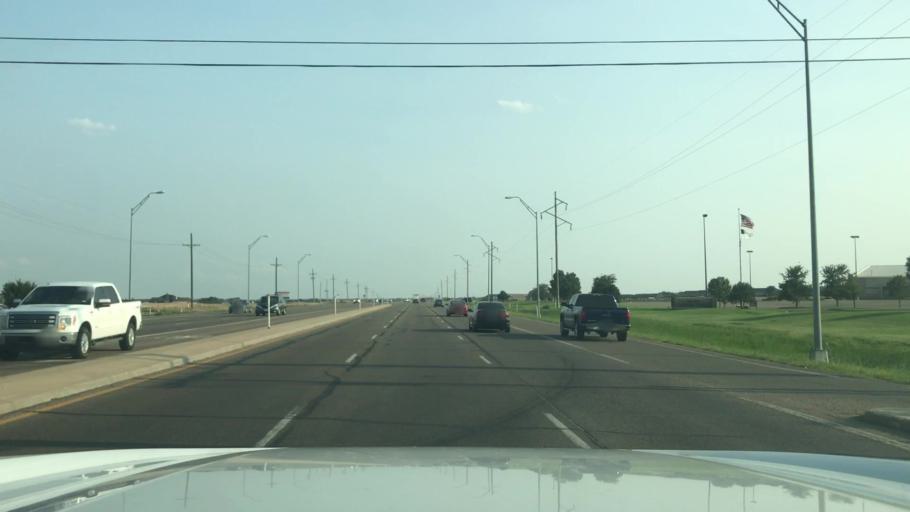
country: US
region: Texas
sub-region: Potter County
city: Amarillo
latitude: 35.1468
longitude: -101.9383
